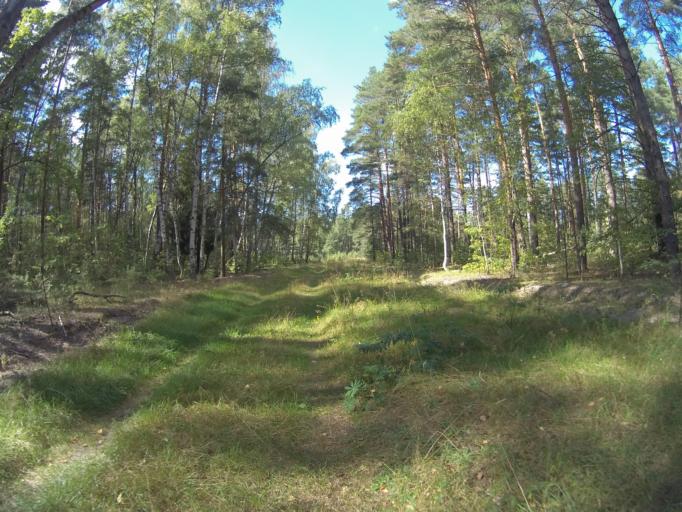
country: RU
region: Vladimir
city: Kommunar
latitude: 56.0588
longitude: 40.4553
